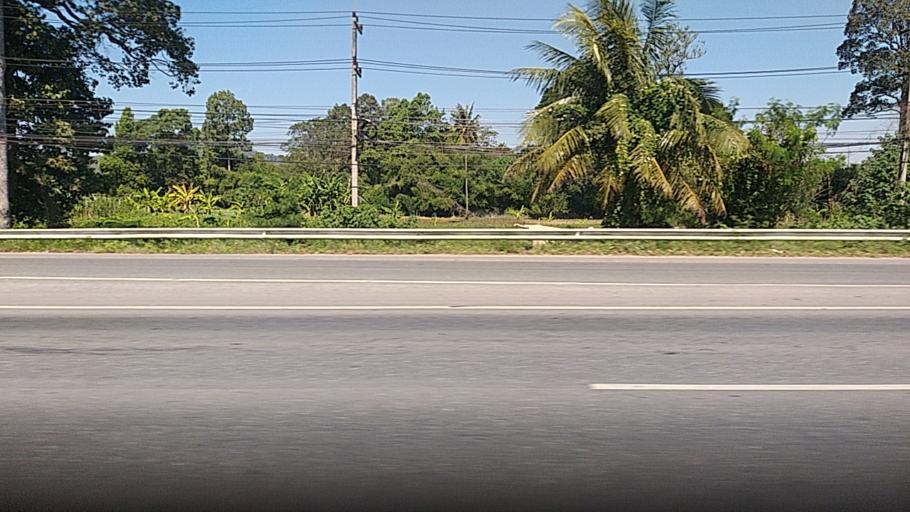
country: TH
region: Nakhon Ratchasima
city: Pak Chong
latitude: 14.6628
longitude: 101.4066
